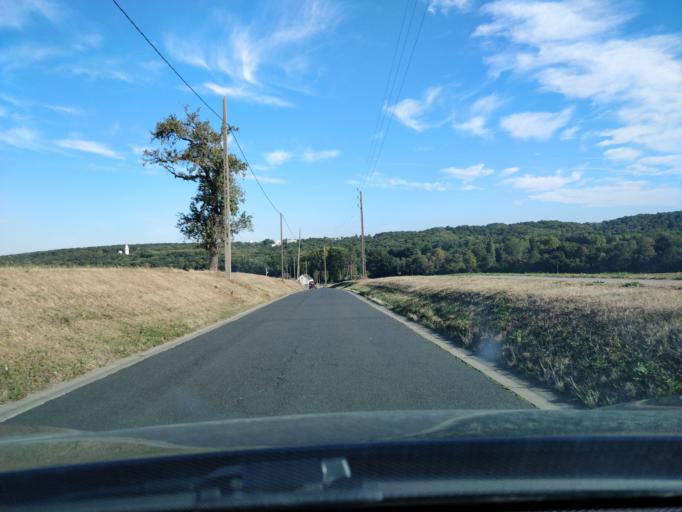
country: FR
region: Ile-de-France
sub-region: Departement de l'Essonne
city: Forges-les-Bains
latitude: 48.6355
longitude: 2.0998
